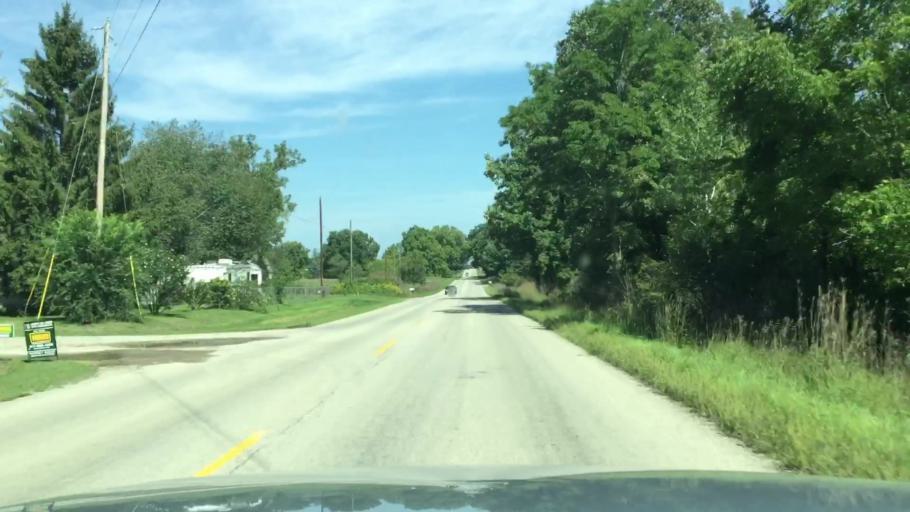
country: US
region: Michigan
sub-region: Lenawee County
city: Manitou Beach-Devils Lake
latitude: 42.0368
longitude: -84.2763
